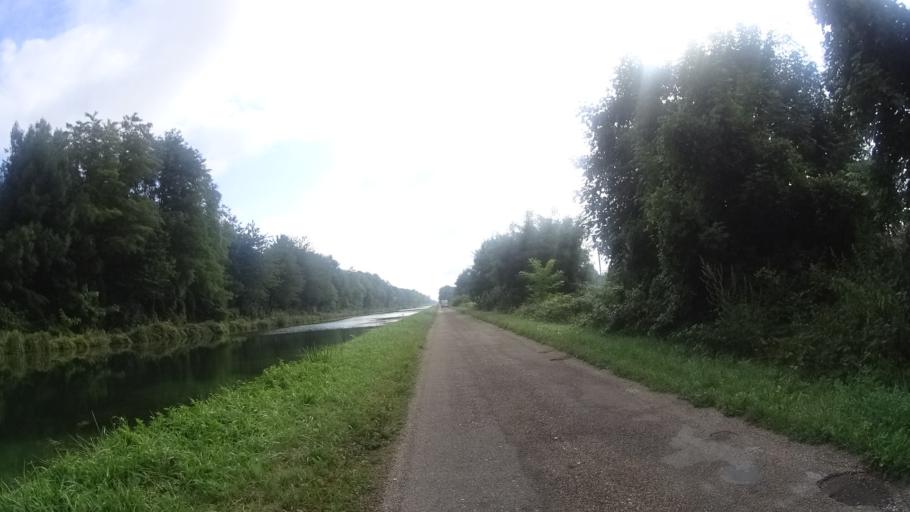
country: FR
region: Bourgogne
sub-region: Departement de l'Yonne
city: Cheny
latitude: 47.9674
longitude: 3.5361
